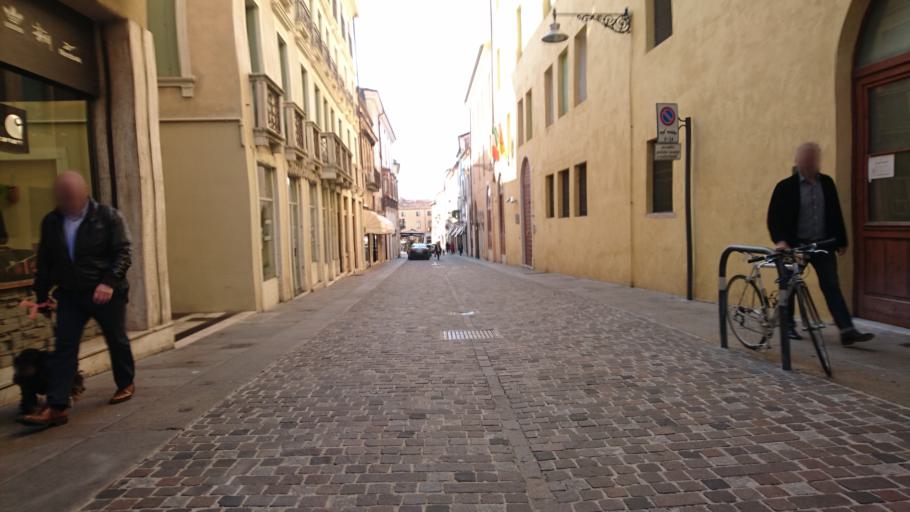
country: IT
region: Veneto
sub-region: Provincia di Vicenza
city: Bassano del Grappa
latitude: 45.7680
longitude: 11.7347
